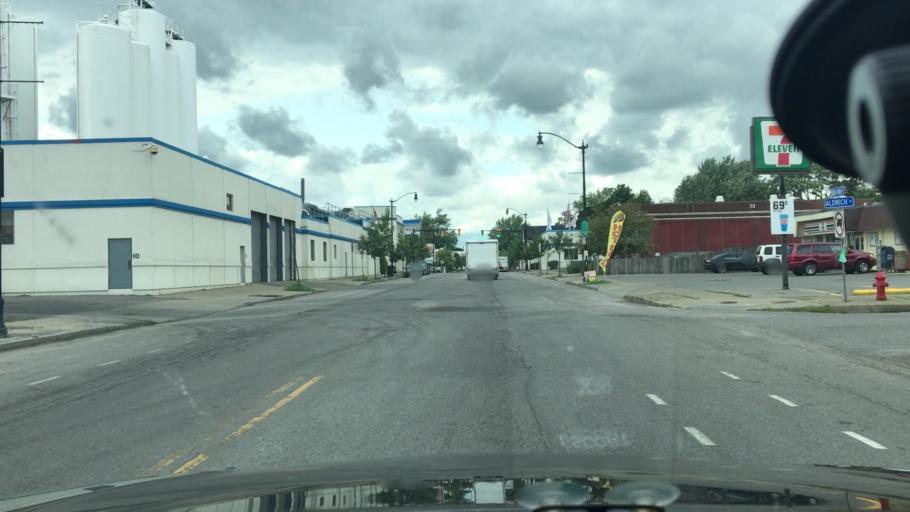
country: US
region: New York
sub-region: Erie County
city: Lackawanna
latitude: 42.8328
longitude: -78.8239
